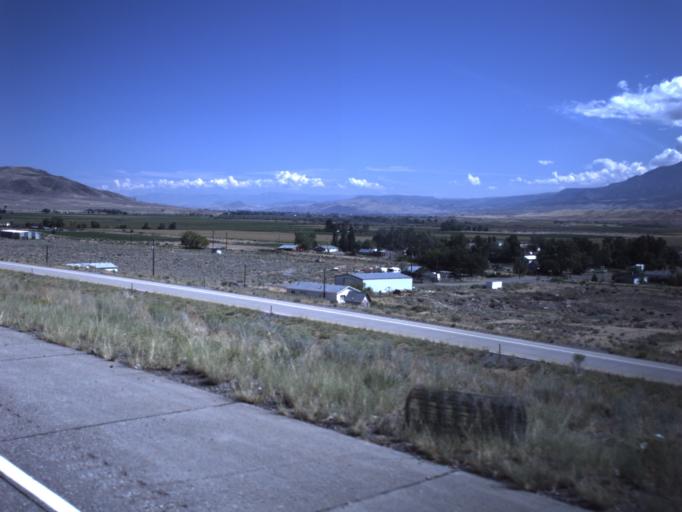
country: US
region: Utah
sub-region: Sevier County
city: Monroe
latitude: 38.6264
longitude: -112.2254
